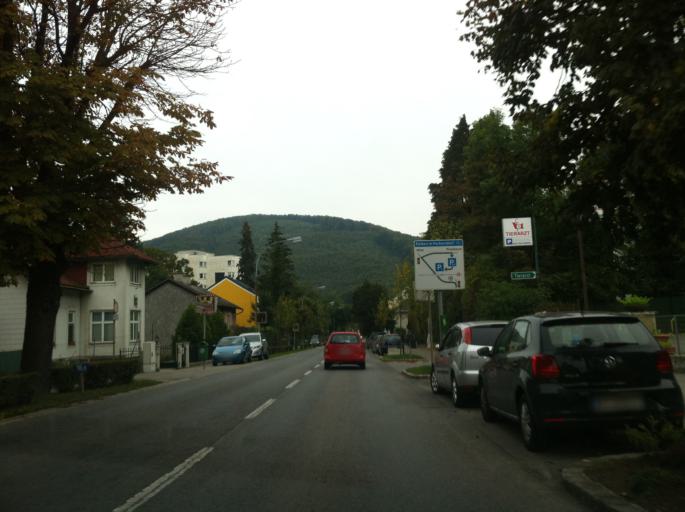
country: AT
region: Lower Austria
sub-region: Politischer Bezirk Wien-Umgebung
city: Purkersdorf
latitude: 48.2107
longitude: 16.1741
